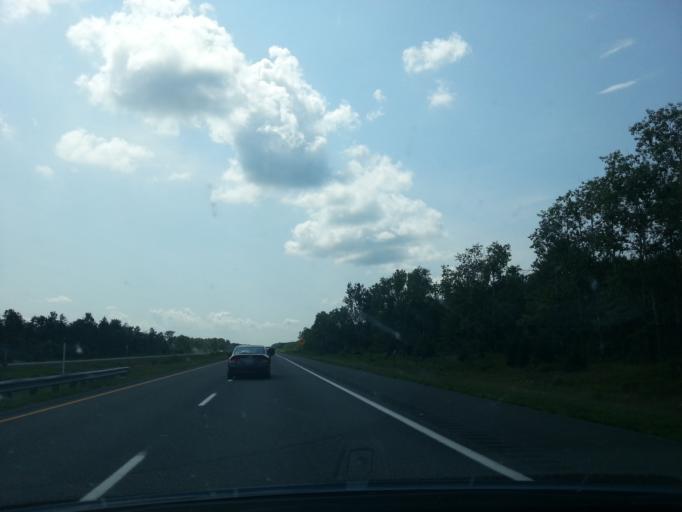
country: CA
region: Quebec
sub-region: Mauricie
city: Daveluyville
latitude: 46.1424
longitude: -72.1776
